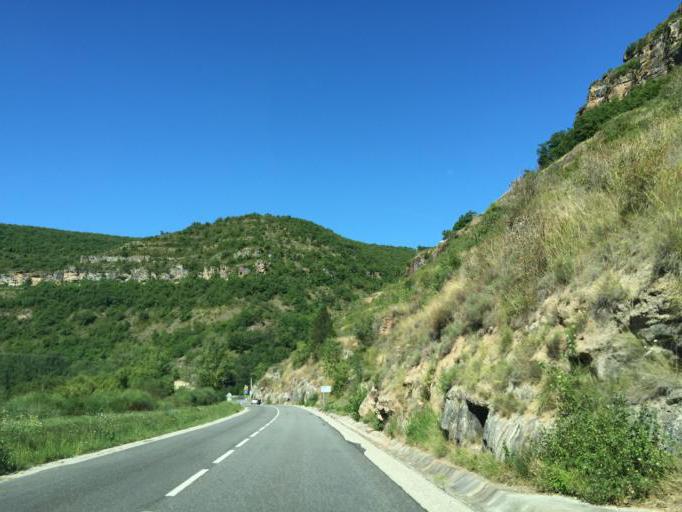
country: FR
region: Midi-Pyrenees
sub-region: Departement de l'Aveyron
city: Saint-Georges-de-Luzencon
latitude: 44.0586
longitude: 2.9053
